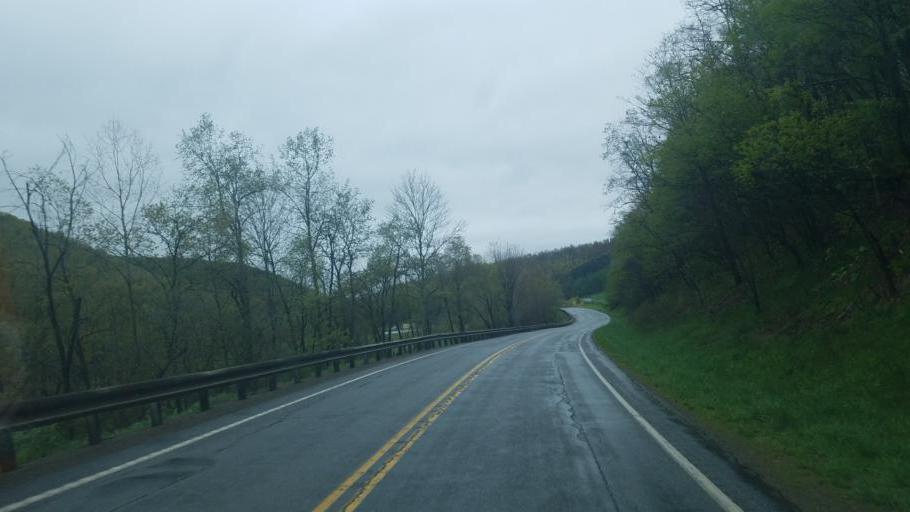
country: US
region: Pennsylvania
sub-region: Potter County
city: Coudersport
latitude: 41.8251
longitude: -77.9605
